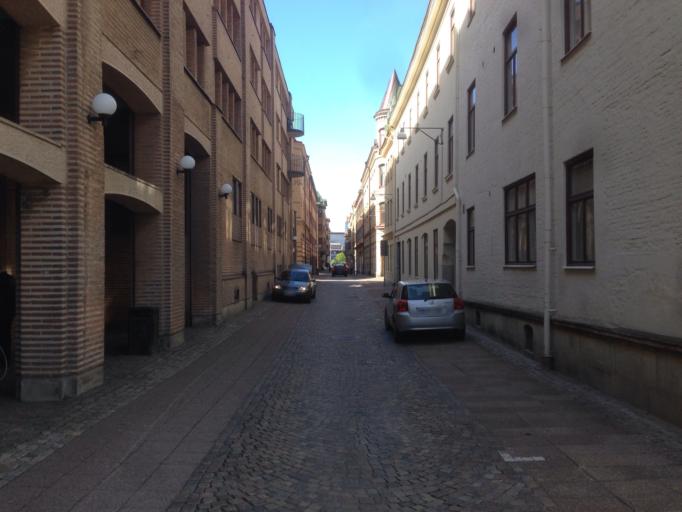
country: SE
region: Vaestra Goetaland
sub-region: Goteborg
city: Goeteborg
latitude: 57.7073
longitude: 11.9659
